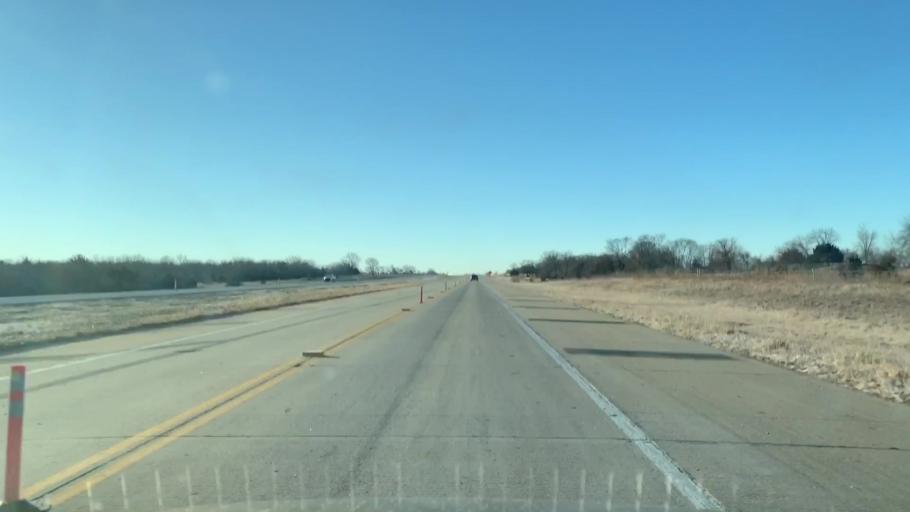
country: US
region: Kansas
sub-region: Bourbon County
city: Fort Scott
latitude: 37.7584
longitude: -94.7050
